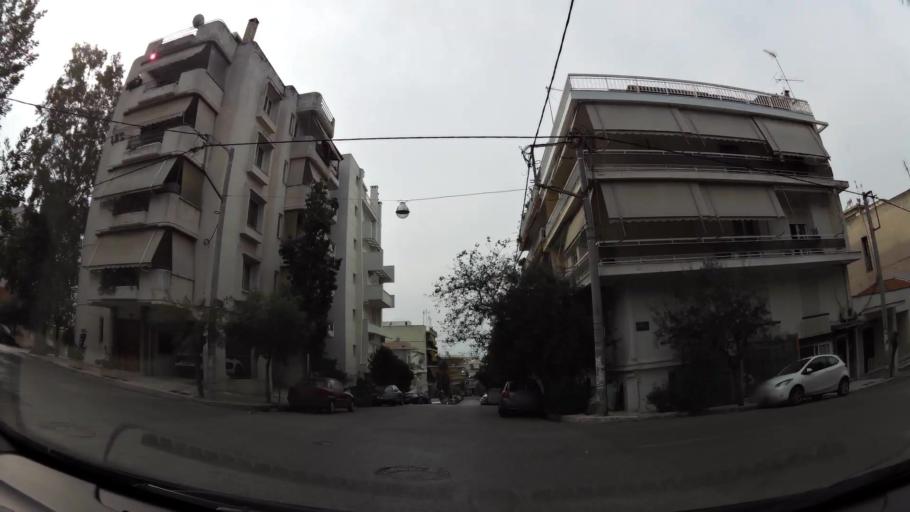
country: GR
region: Attica
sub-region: Nomarchia Athinas
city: Nea Ionia
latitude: 38.0309
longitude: 23.7479
